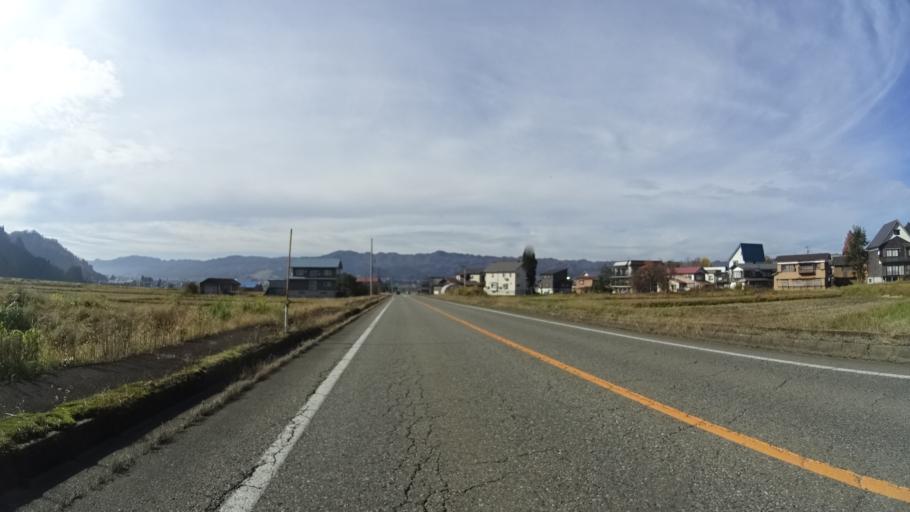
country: JP
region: Niigata
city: Muikamachi
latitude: 37.1288
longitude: 138.9419
